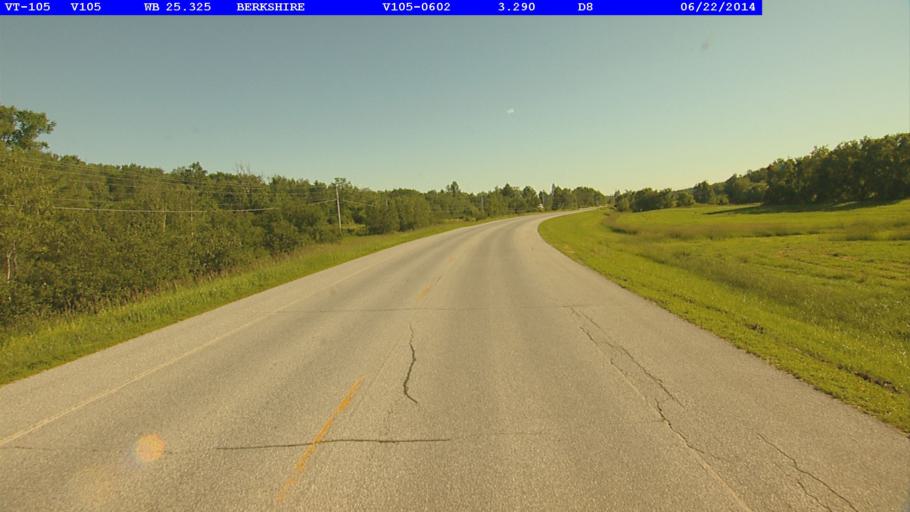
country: US
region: Vermont
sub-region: Franklin County
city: Richford
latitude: 44.9656
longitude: -72.6900
